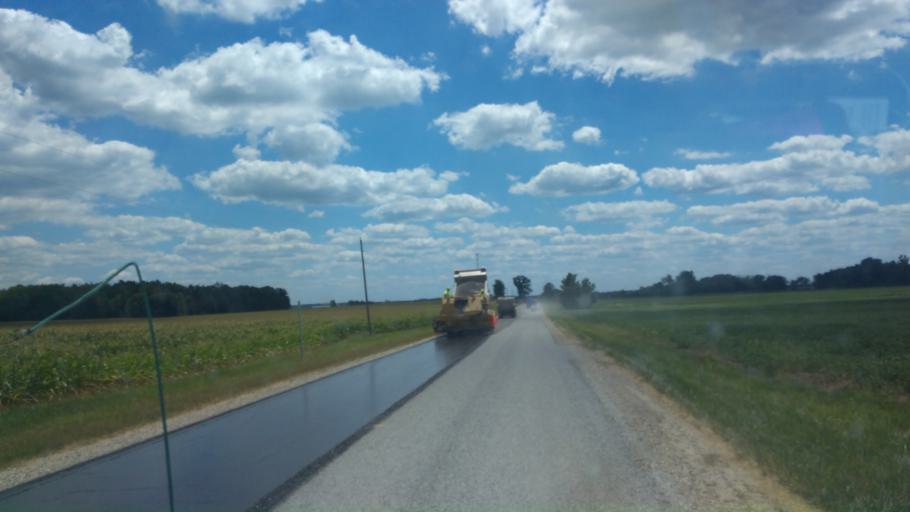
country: US
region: Indiana
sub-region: Adams County
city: Geneva
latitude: 40.6026
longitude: -85.0408
